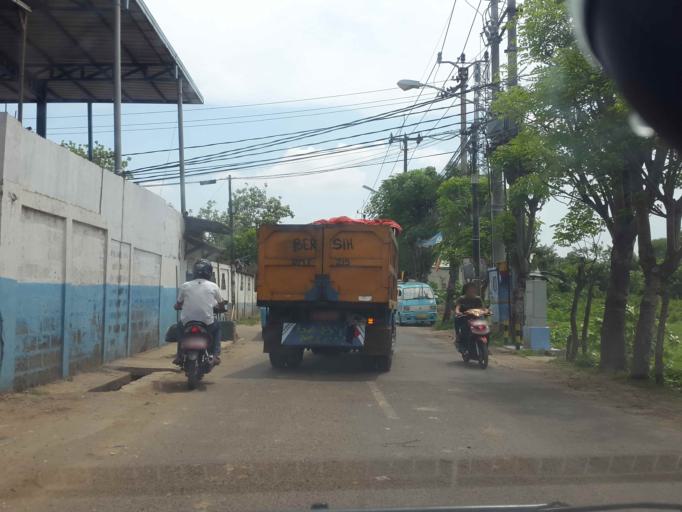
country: ID
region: Banten
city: Tangerang
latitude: -6.1429
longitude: 106.6184
